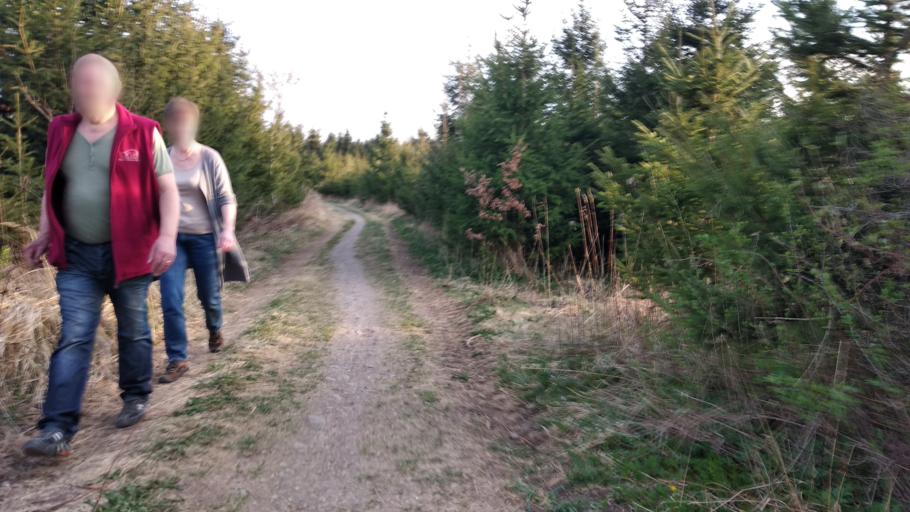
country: DE
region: Bavaria
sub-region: Upper Bavaria
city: Haar
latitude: 48.1031
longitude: 11.7445
